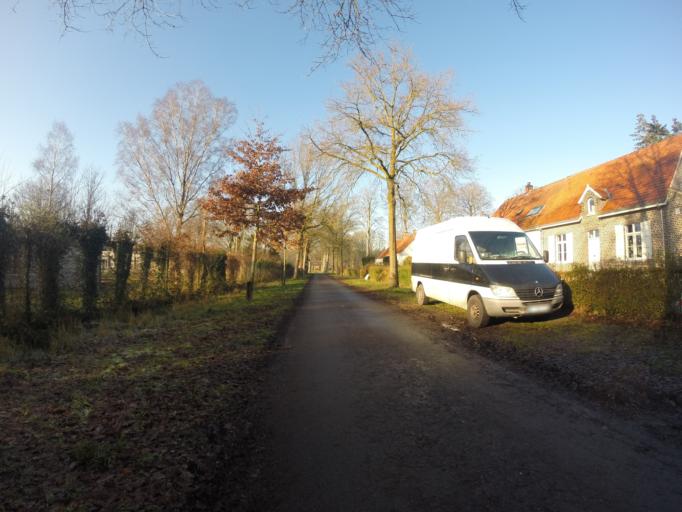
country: BE
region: Flanders
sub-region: Provincie West-Vlaanderen
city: Beernem
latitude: 51.0878
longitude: 3.3374
